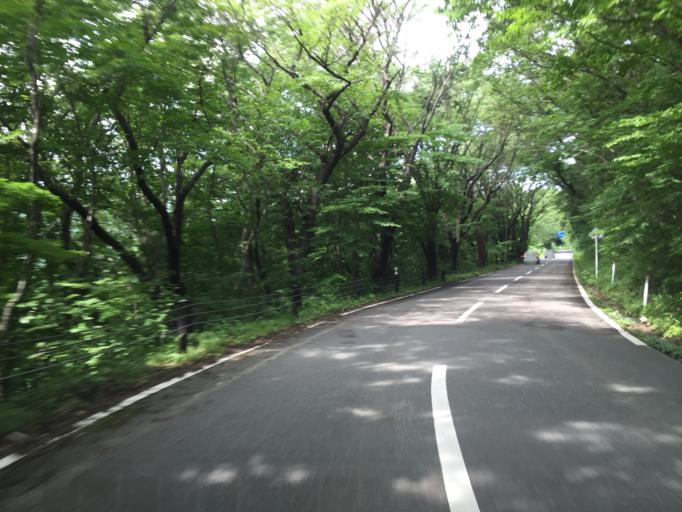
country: JP
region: Fukushima
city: Nihommatsu
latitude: 37.6794
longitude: 140.3309
